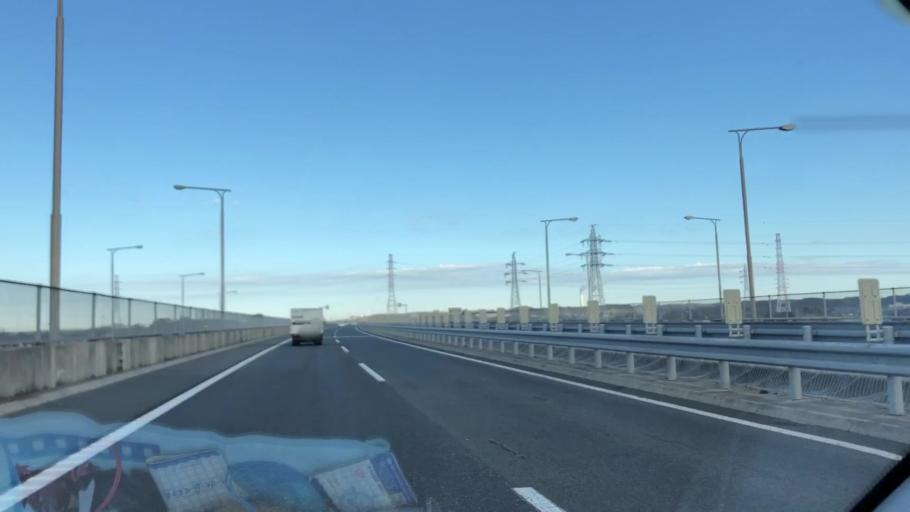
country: JP
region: Chiba
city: Kisarazu
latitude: 35.3938
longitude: 139.9688
